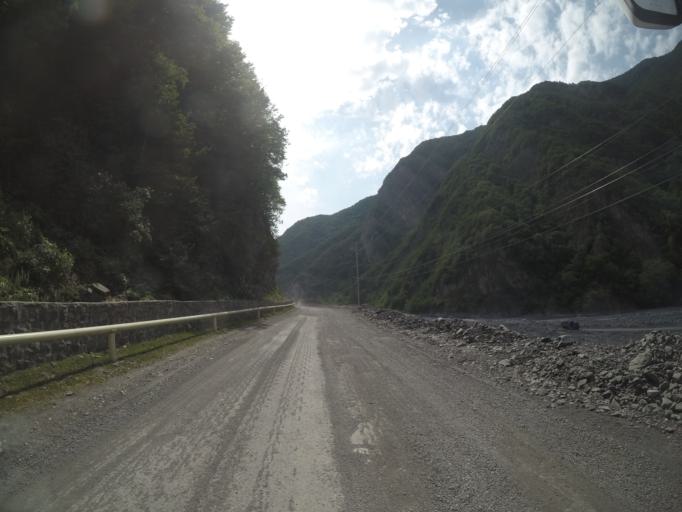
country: AZ
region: Qakh Rayon
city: Qaxbas
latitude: 41.4636
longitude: 47.0345
